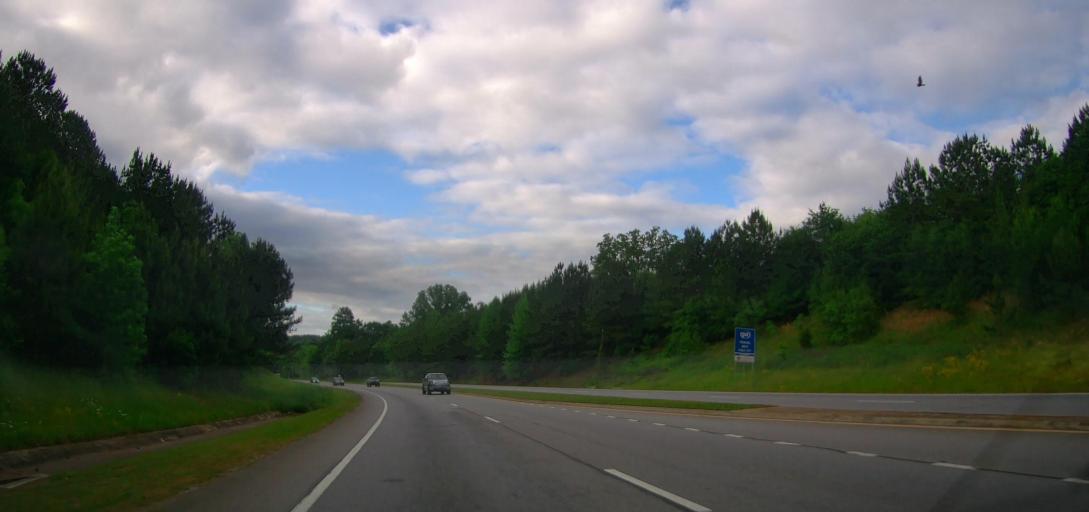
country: US
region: Georgia
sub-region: Oconee County
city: Watkinsville
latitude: 33.9054
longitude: -83.4044
